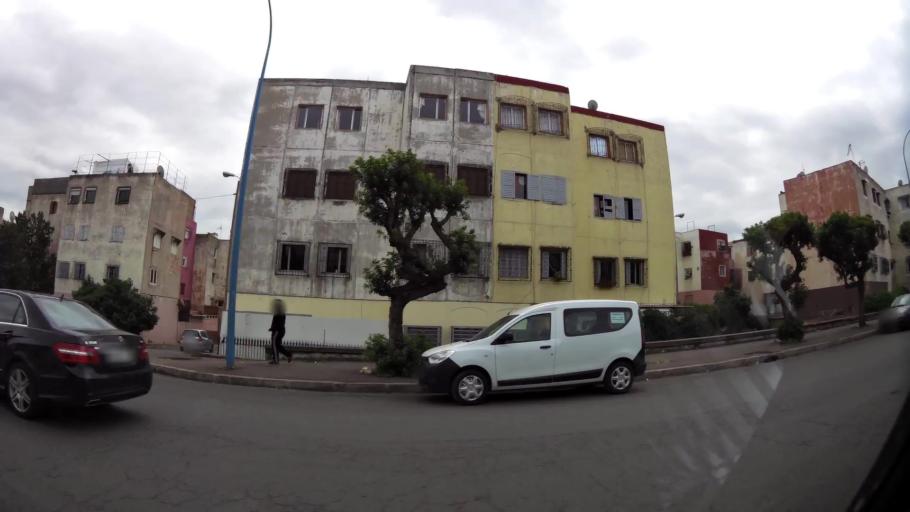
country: MA
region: Grand Casablanca
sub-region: Casablanca
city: Casablanca
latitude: 33.5772
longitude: -7.5656
